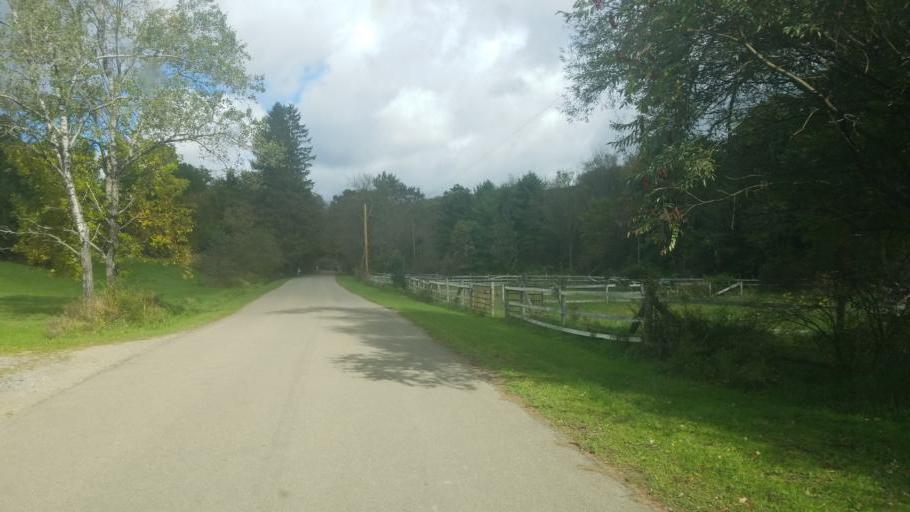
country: US
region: New York
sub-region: Cattaraugus County
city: Weston Mills
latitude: 42.1441
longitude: -78.3509
